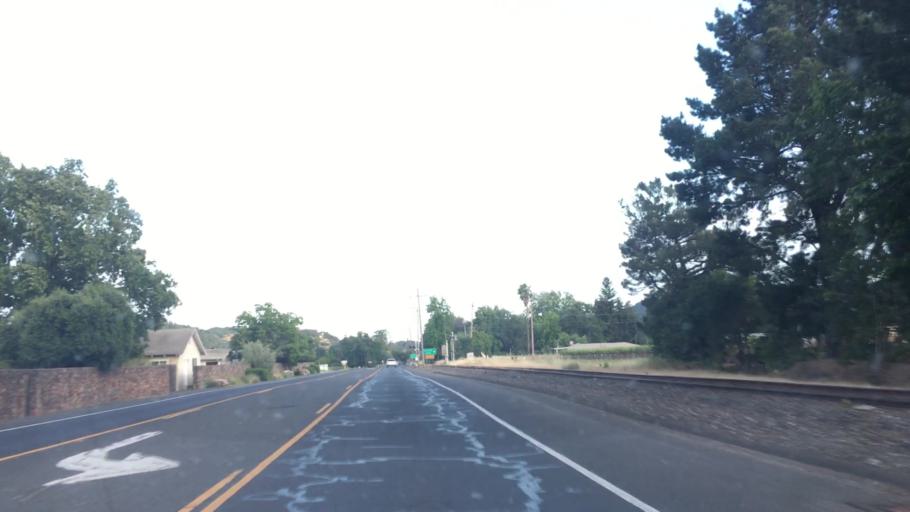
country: US
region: California
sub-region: Napa County
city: Yountville
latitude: 38.4358
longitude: -122.4018
